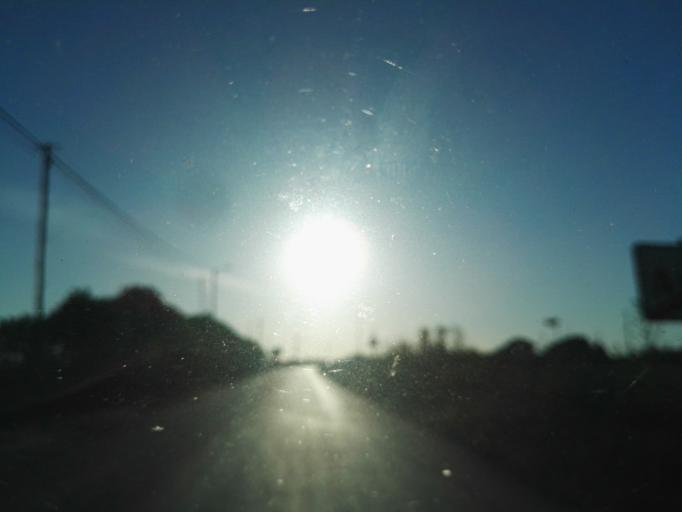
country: PT
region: Santarem
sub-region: Golega
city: Golega
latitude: 39.3443
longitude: -8.5337
